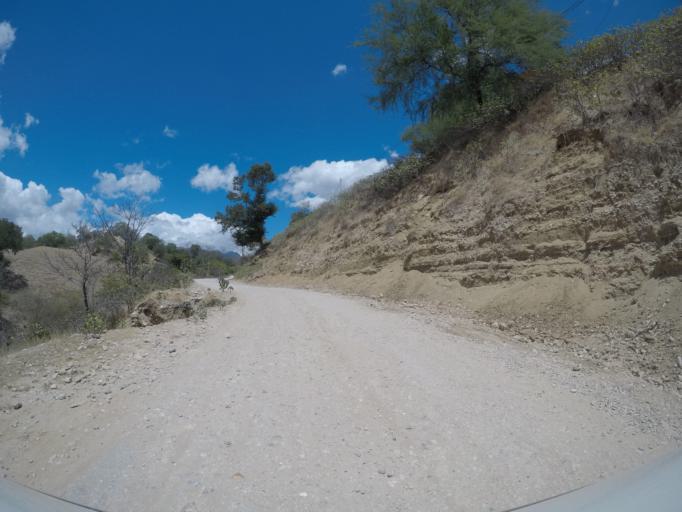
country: TL
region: Baucau
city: Baucau
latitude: -8.4749
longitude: 126.6007
